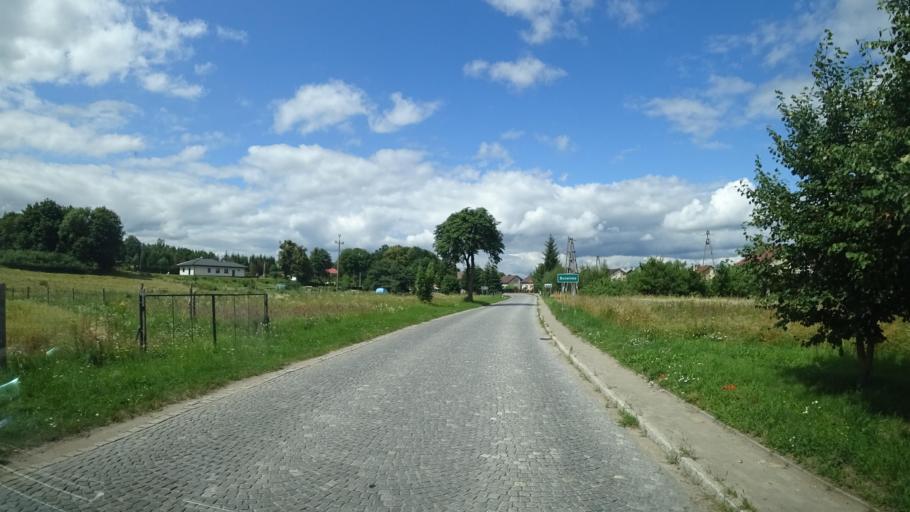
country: PL
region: Warmian-Masurian Voivodeship
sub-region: Powiat goldapski
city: Banie Mazurskie
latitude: 54.2159
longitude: 22.1564
